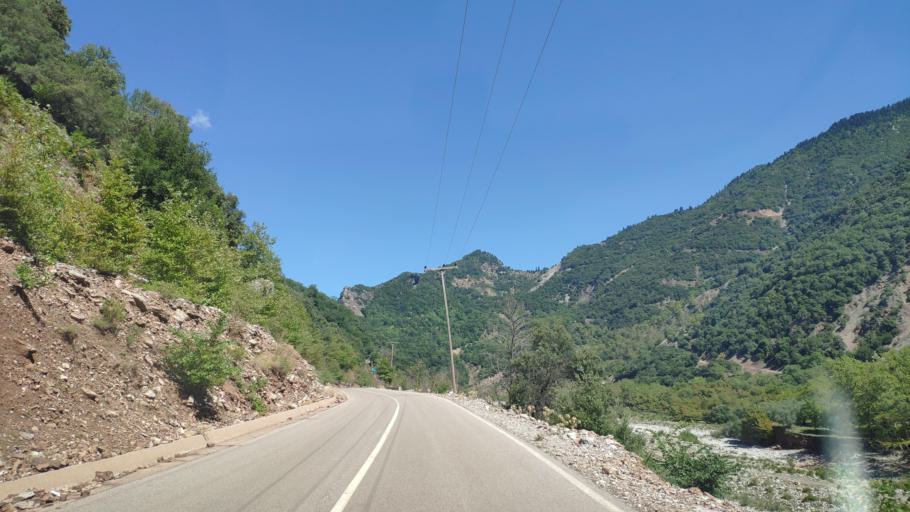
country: GR
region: Central Greece
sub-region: Nomos Evrytanias
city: Kerasochori
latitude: 39.0596
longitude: 21.6072
